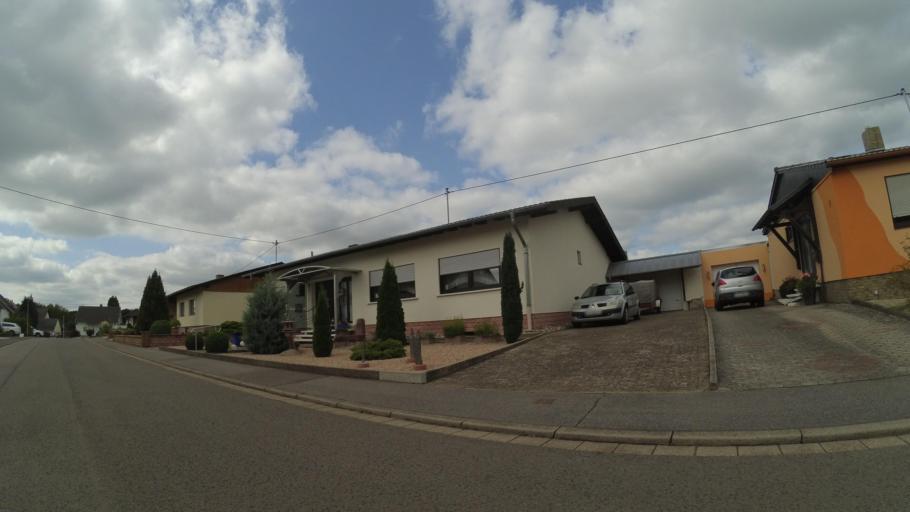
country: FR
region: Lorraine
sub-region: Departement de la Moselle
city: Carling
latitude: 49.1858
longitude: 6.7346
